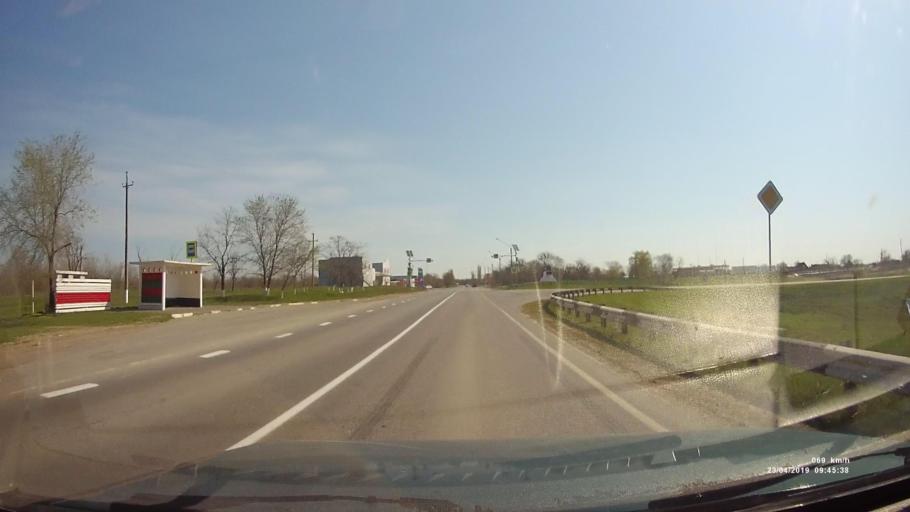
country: RU
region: Rostov
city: Orlovskiy
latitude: 46.8848
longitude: 42.0337
